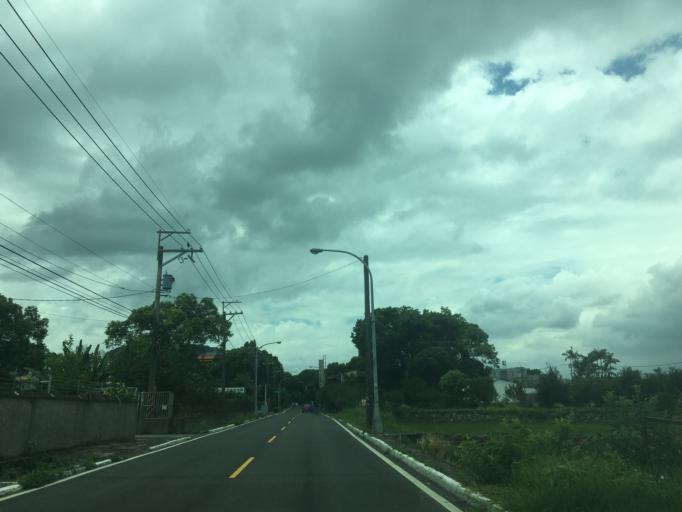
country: TW
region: Taiwan
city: Daxi
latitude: 24.8525
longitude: 121.2897
